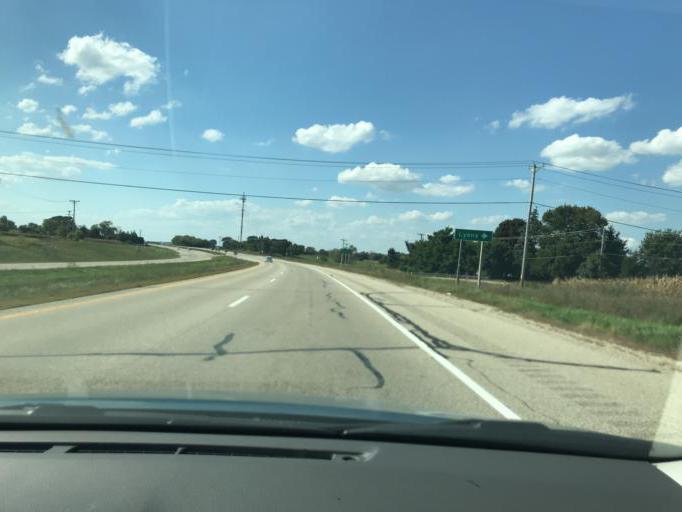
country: US
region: Wisconsin
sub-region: Walworth County
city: Pell Lake
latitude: 42.5954
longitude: -88.3514
